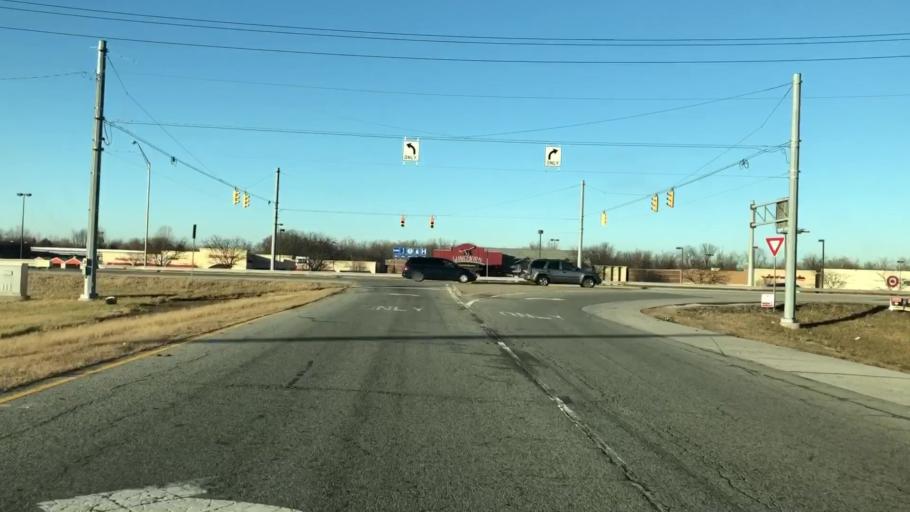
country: US
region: Indiana
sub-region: Marion County
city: Southport
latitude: 39.6653
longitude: -86.0864
